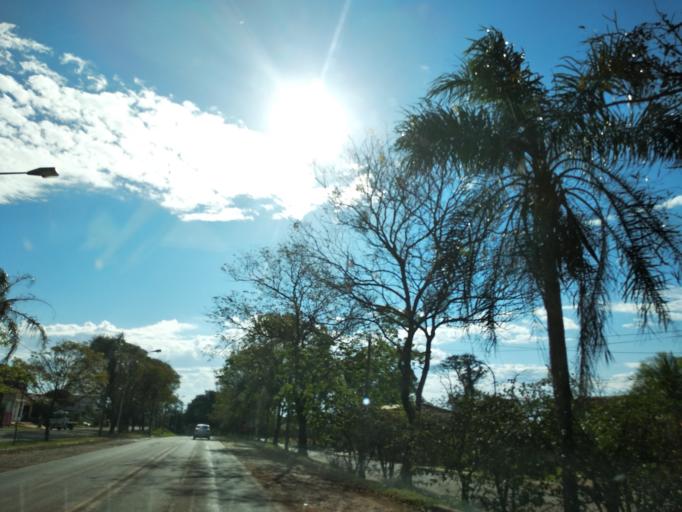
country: AR
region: Misiones
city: Aristobulo del Valle
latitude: -27.0936
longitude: -54.8957
